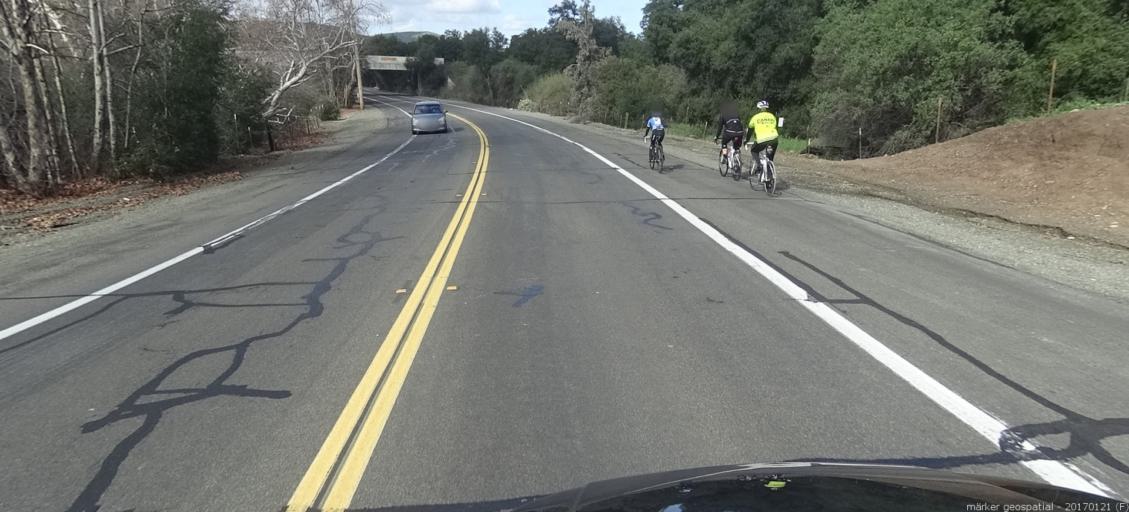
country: US
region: California
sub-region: Orange County
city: Foothill Ranch
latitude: 33.7591
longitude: -117.7013
